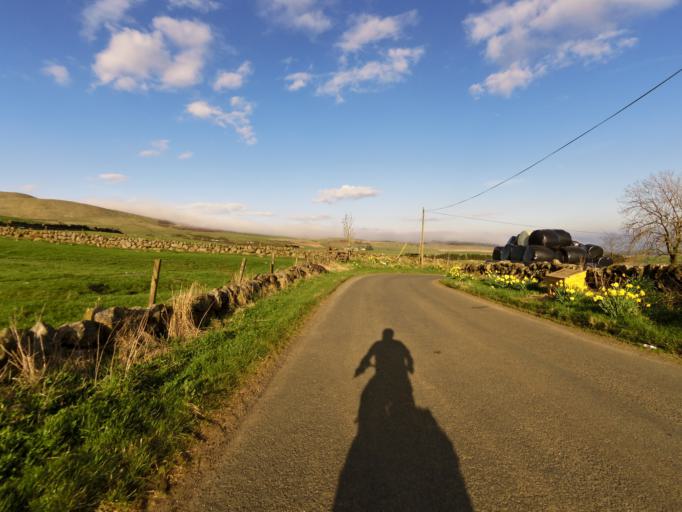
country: GB
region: Scotland
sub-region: Fife
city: Falkland
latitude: 56.2332
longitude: -3.2313
